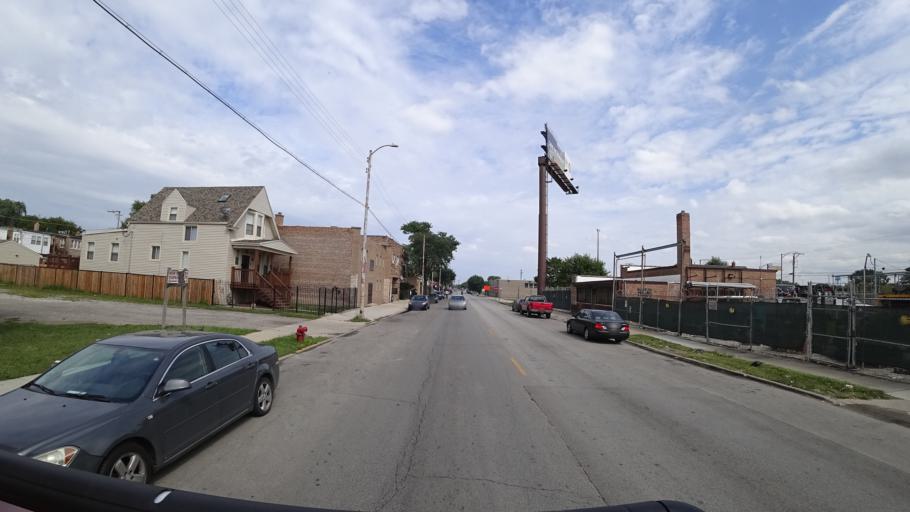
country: US
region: Illinois
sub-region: Cook County
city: Cicero
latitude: 41.8730
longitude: -87.7584
